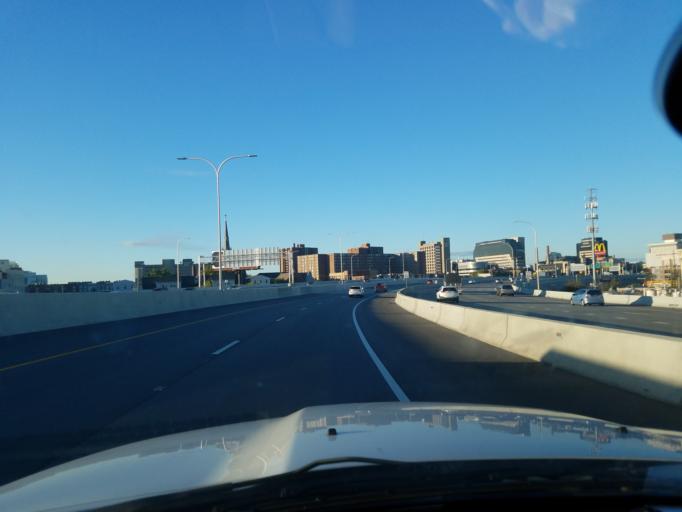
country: US
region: Kentucky
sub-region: Jefferson County
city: Louisville
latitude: 38.2546
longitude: -85.7426
